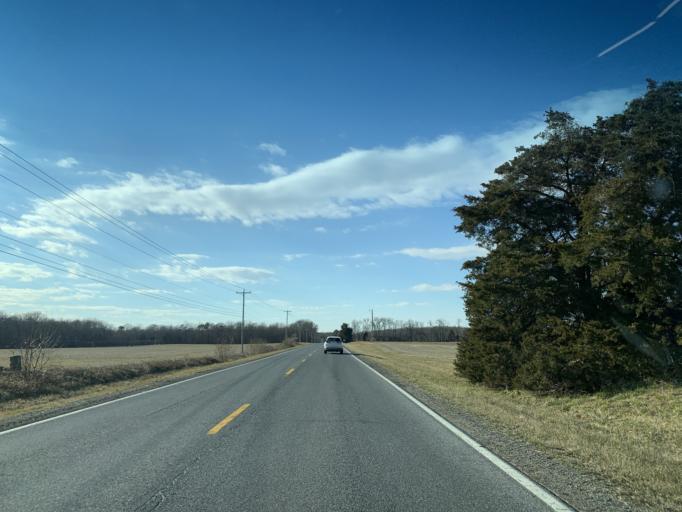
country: US
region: Maryland
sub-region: Queen Anne's County
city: Centreville
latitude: 39.0216
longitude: -76.0114
